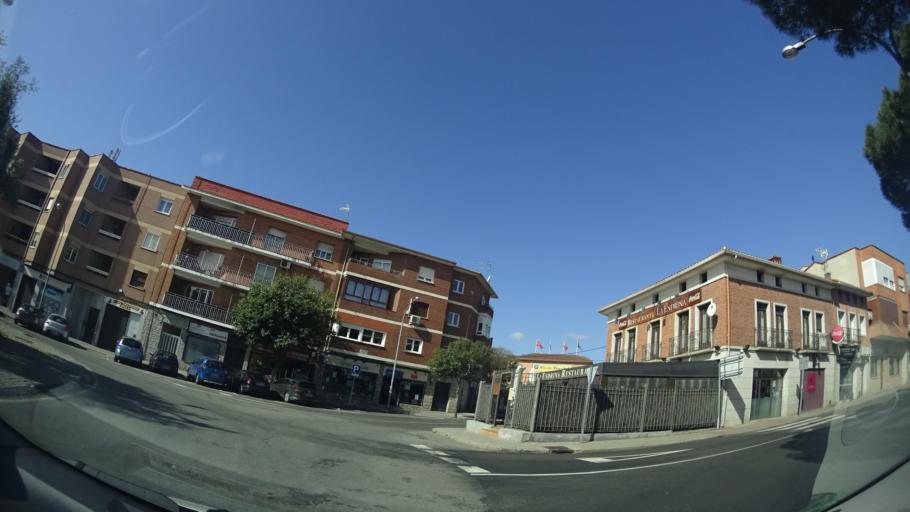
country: ES
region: Madrid
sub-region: Provincia de Madrid
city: Colmenar Viejo
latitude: 40.6654
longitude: -3.7699
